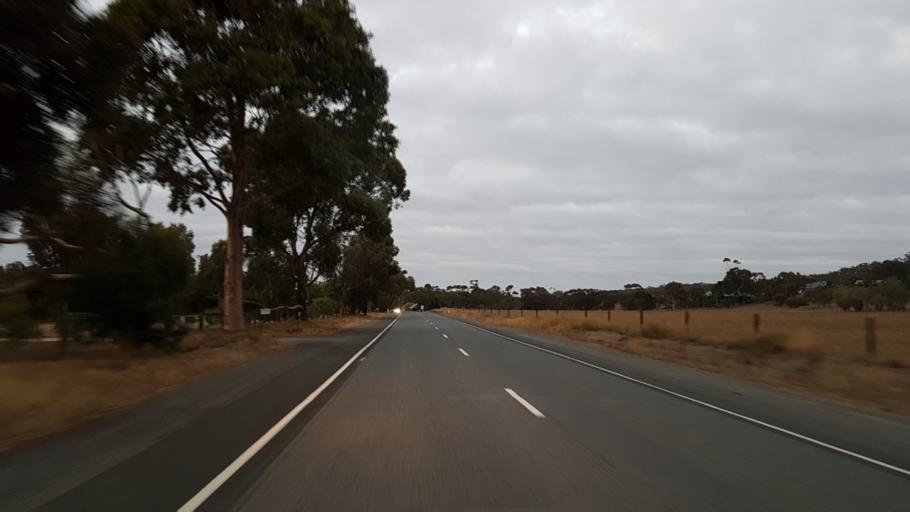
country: AU
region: South Australia
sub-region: Mount Barker
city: Callington
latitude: -35.0642
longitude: 139.0123
